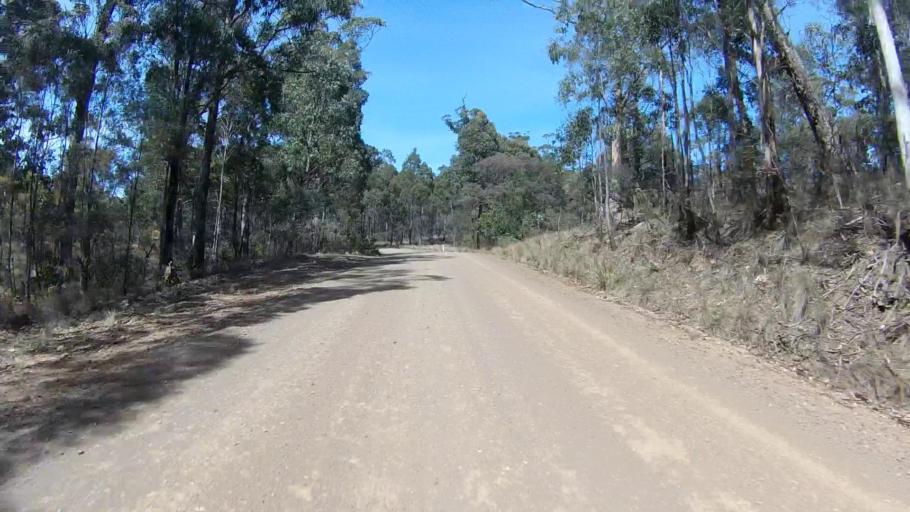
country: AU
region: Tasmania
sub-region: Sorell
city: Sorell
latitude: -42.6643
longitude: 147.7300
